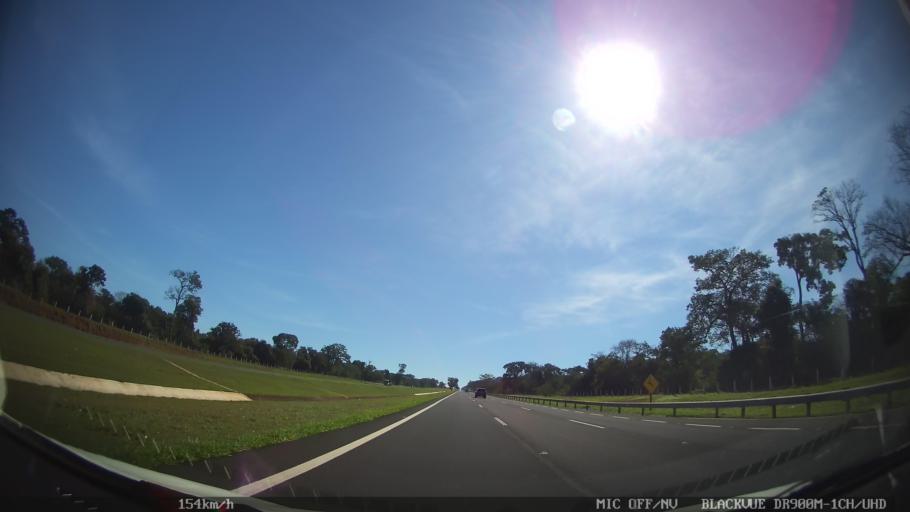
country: BR
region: Sao Paulo
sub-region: Santa Rita Do Passa Quatro
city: Santa Rita do Passa Quatro
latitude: -21.7270
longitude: -47.5862
